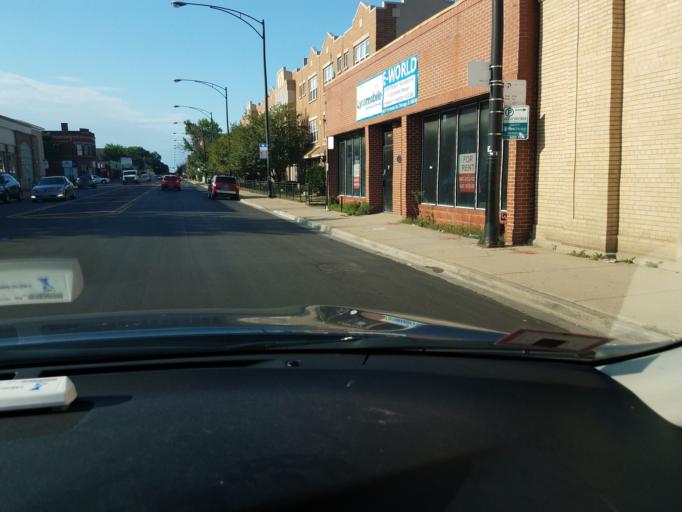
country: US
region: Illinois
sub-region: Cook County
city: Lincolnwood
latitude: 41.9692
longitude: -87.7280
